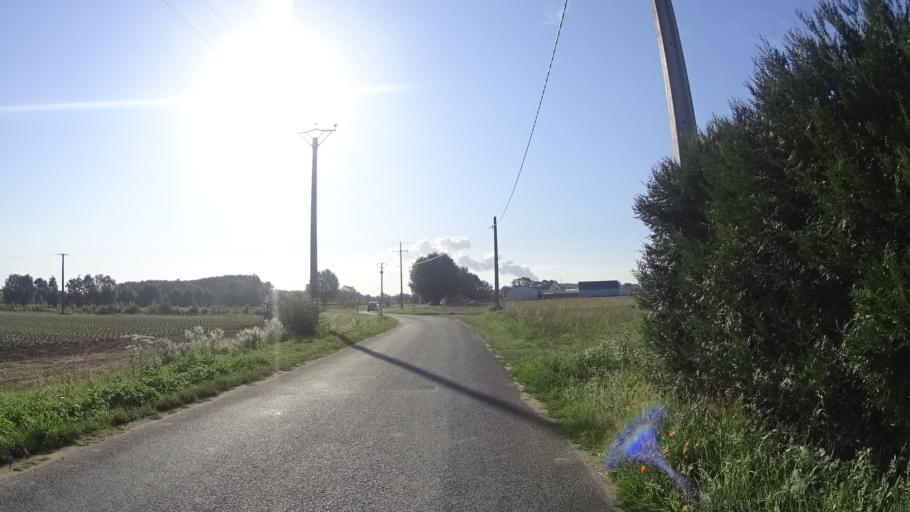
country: FR
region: Pays de la Loire
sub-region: Departement de Maine-et-Loire
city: Allonnes
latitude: 47.2649
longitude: 0.0106
